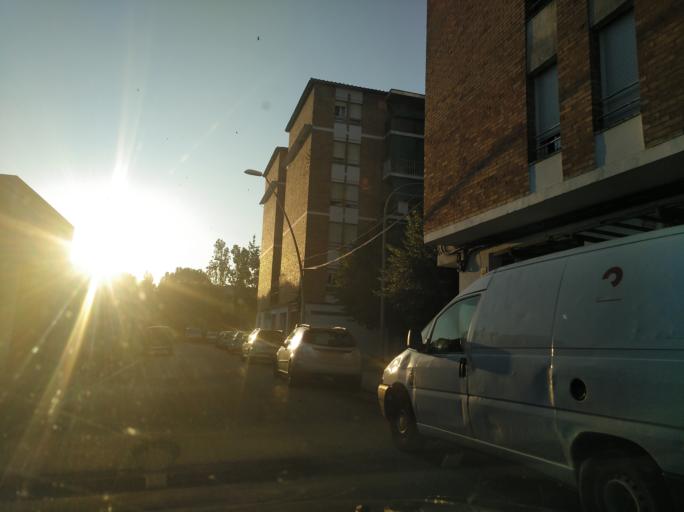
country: ES
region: Catalonia
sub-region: Provincia de Girona
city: Salt
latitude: 41.9714
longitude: 2.7897
